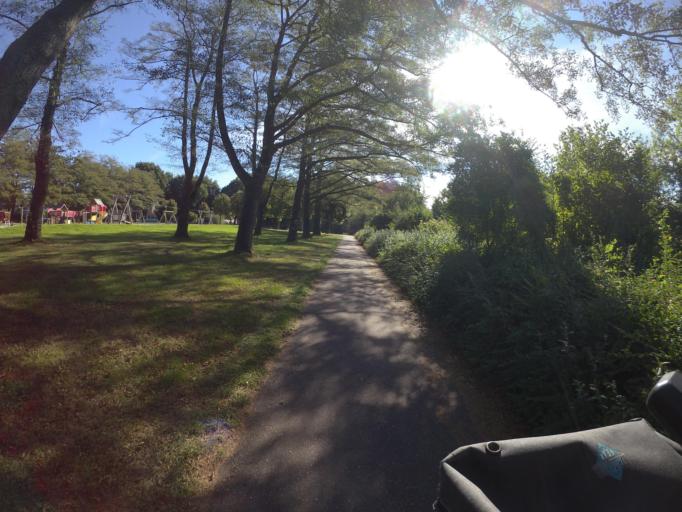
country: NL
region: Drenthe
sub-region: Gemeente Hoogeveen
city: Hoogeveen
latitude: 52.7111
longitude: 6.4825
